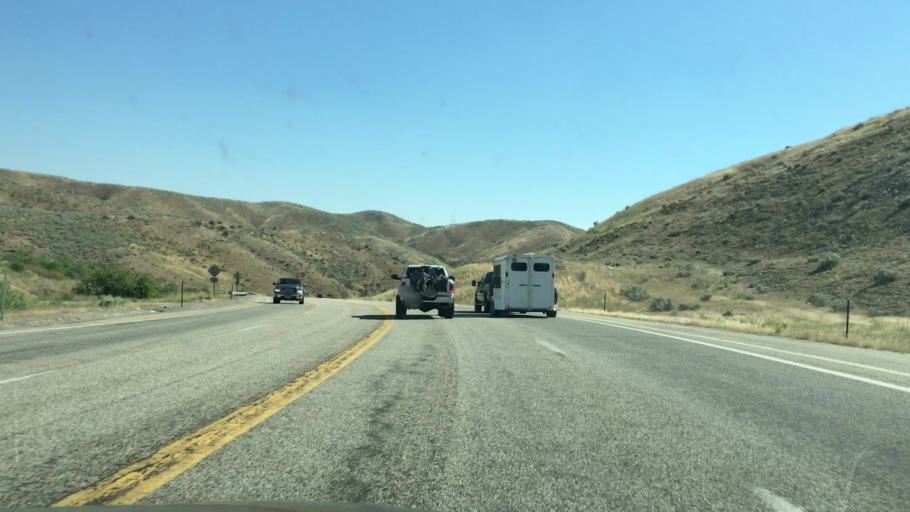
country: US
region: Idaho
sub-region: Ada County
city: Eagle
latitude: 43.8352
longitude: -116.2454
